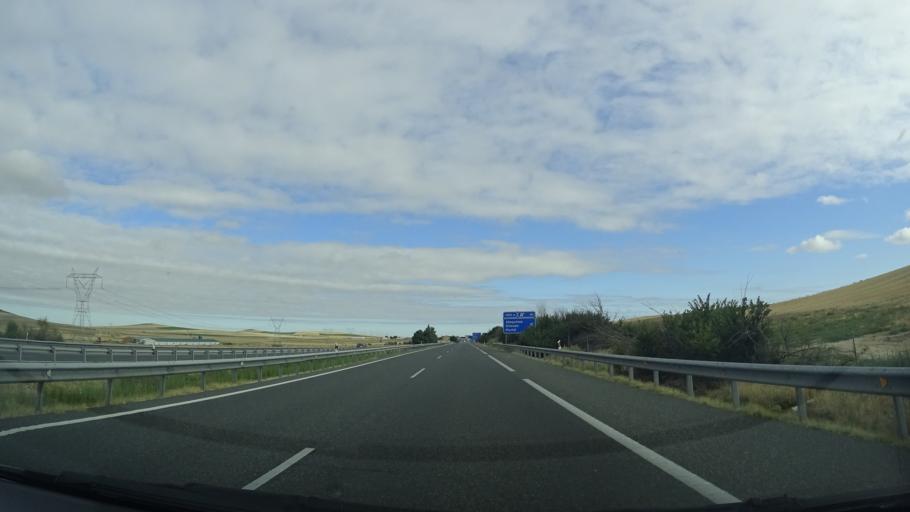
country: ES
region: Castille and Leon
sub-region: Provincia de Valladolid
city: Ataquines
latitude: 41.1645
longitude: -4.7990
